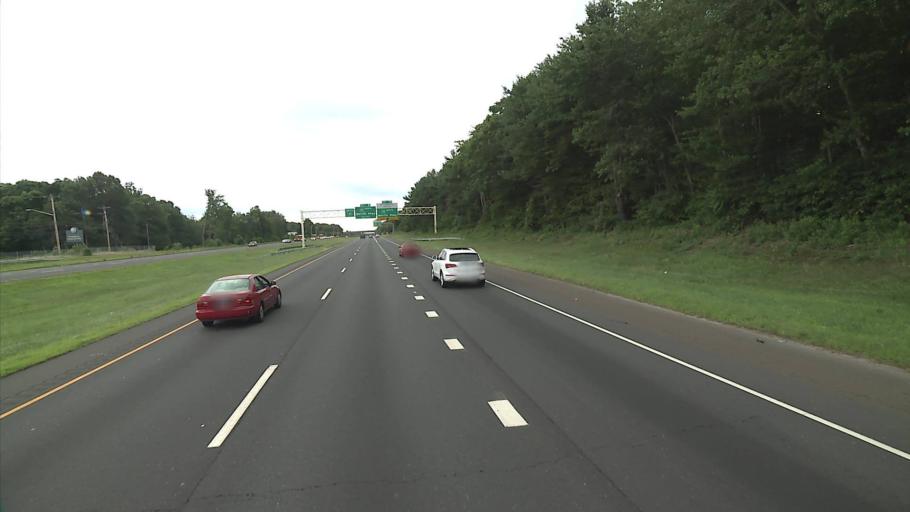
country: US
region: Connecticut
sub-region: Fairfield County
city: Trumbull
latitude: 41.2462
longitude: -73.1504
